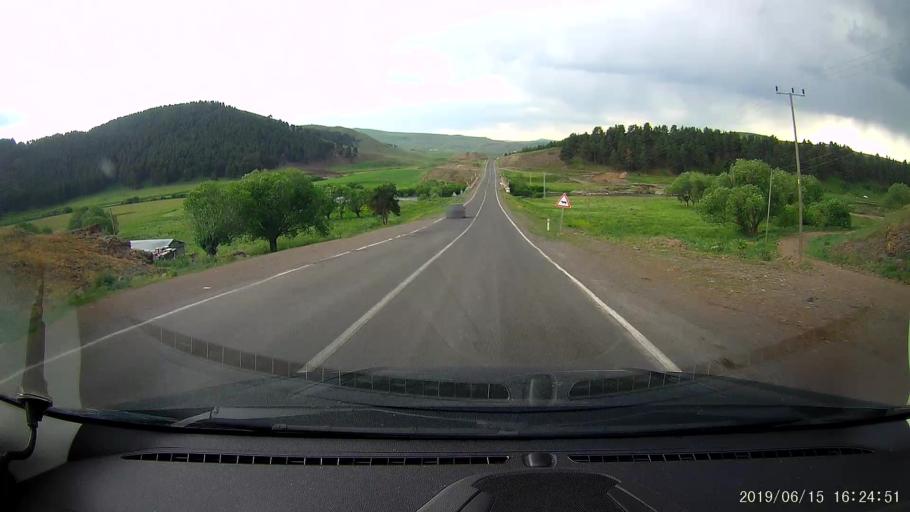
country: TR
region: Ardahan
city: Hanak
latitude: 41.1614
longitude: 42.8725
